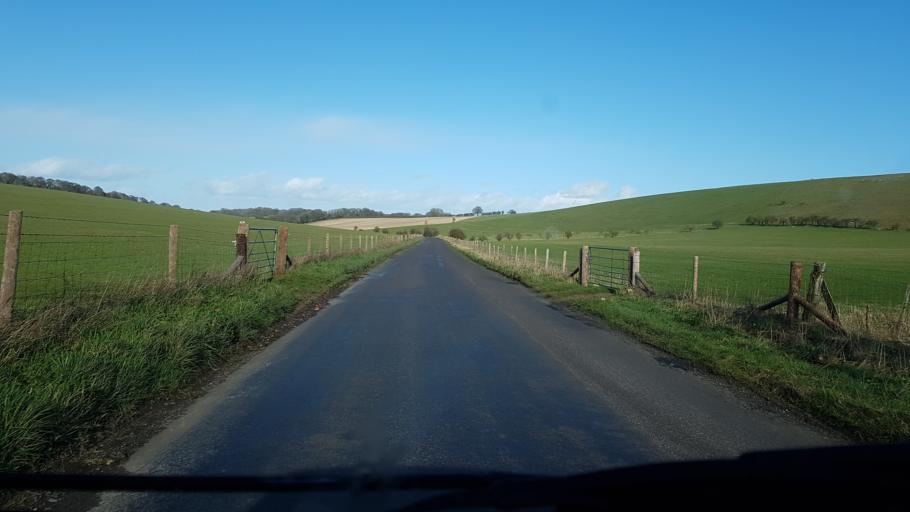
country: GB
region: England
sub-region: Wiltshire
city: Huish
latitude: 51.3769
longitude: -1.8297
